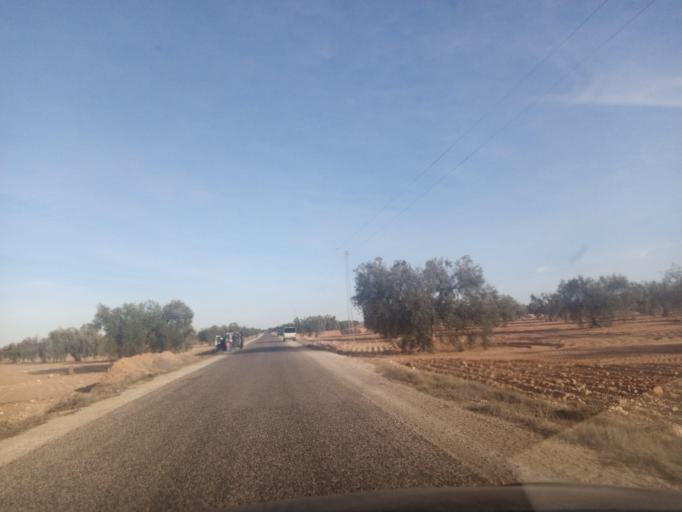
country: TN
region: Safaqis
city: Bi'r `Ali Bin Khalifah
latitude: 34.8877
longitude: 10.1833
